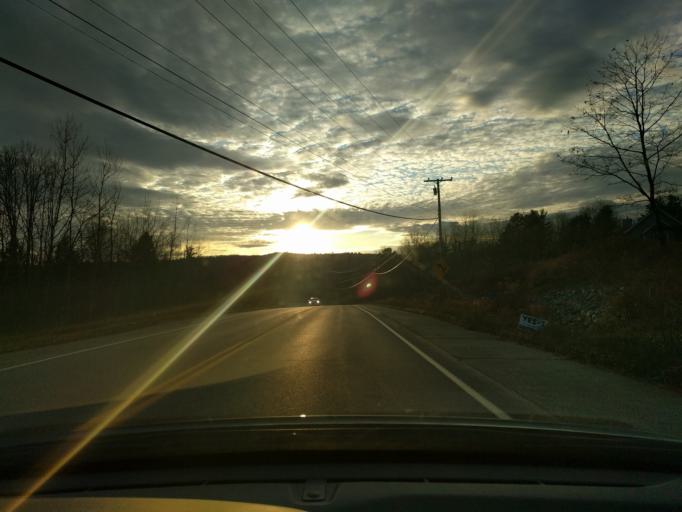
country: US
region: Maine
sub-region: Waldo County
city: Frankfort
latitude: 44.6288
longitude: -68.8656
